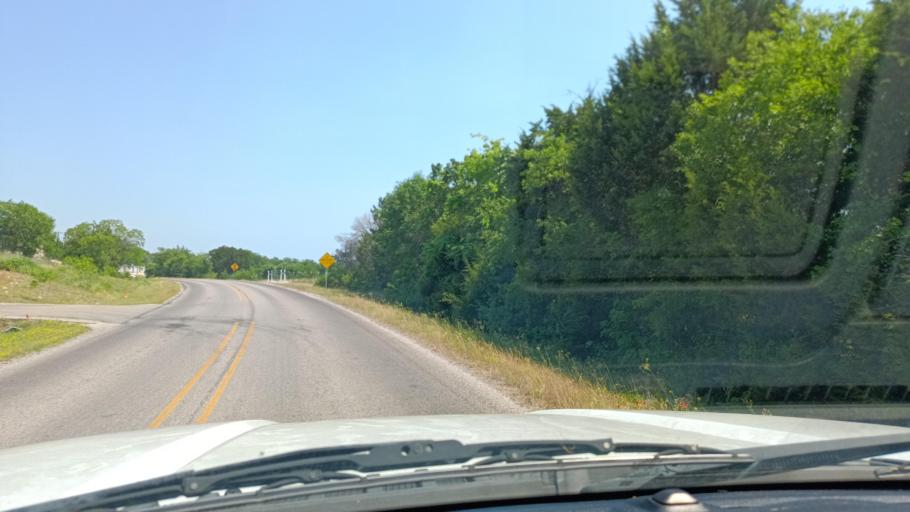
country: US
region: Texas
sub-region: Bell County
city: Belton
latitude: 31.1019
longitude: -97.5185
